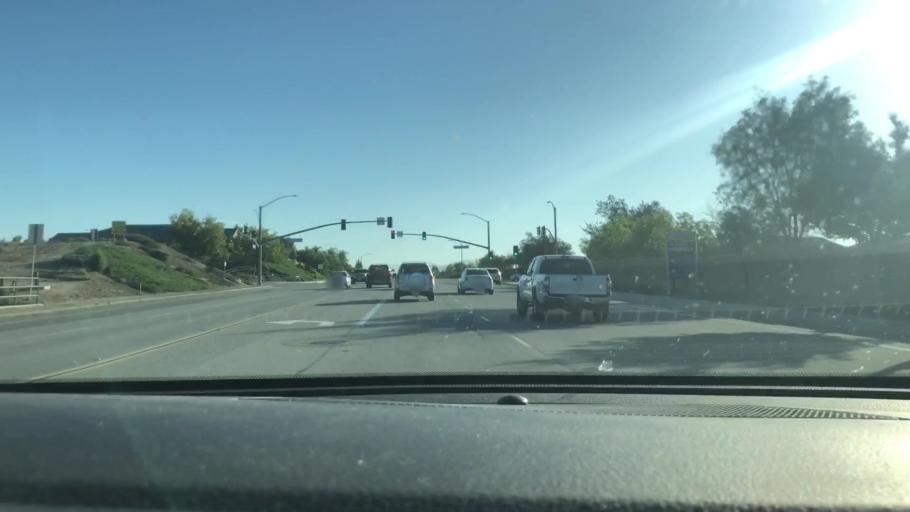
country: US
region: California
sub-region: Riverside County
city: Murrieta Hot Springs
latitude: 33.5964
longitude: -117.1879
